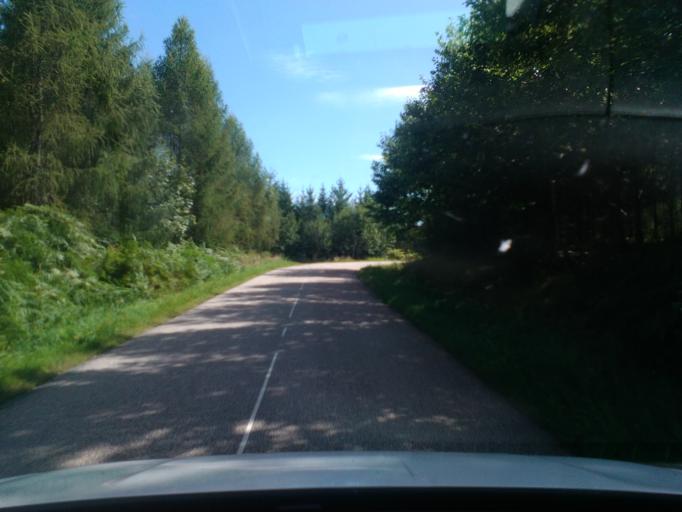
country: FR
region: Lorraine
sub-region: Departement des Vosges
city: Senones
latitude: 48.3708
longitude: 6.9730
